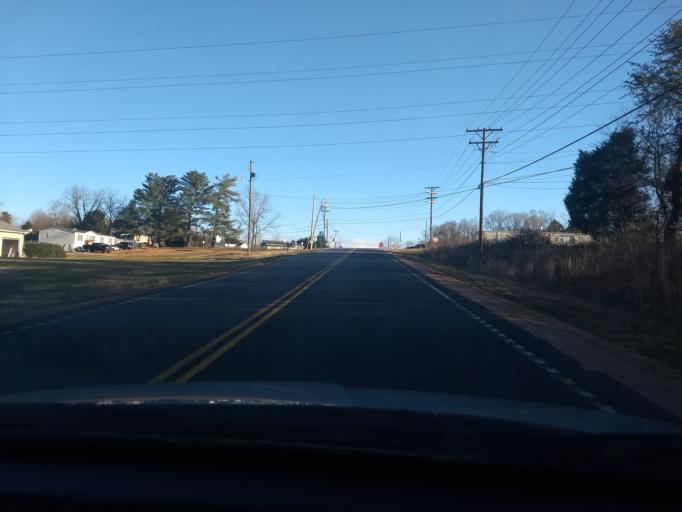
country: US
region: South Carolina
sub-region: Greenville County
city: Greer
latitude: 34.9761
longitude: -82.1949
